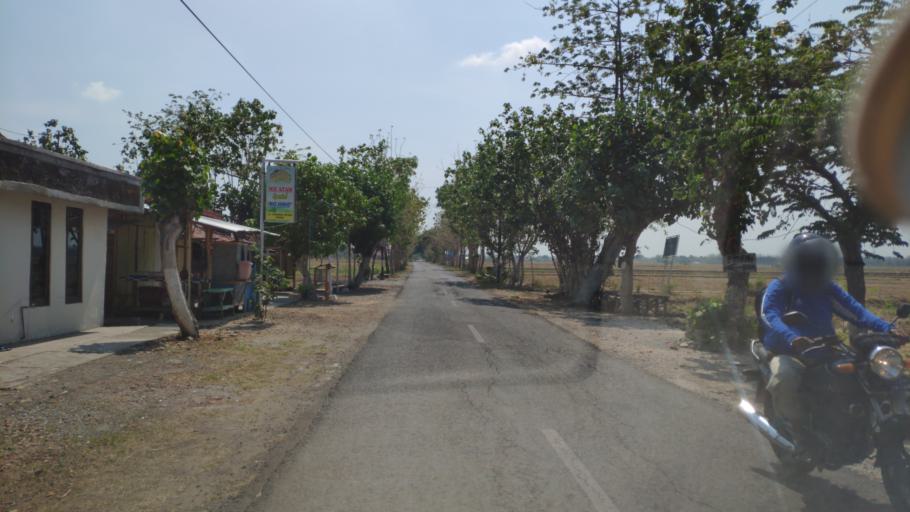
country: ID
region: Central Java
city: Kedungjenar
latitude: -6.9800
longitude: 111.4240
